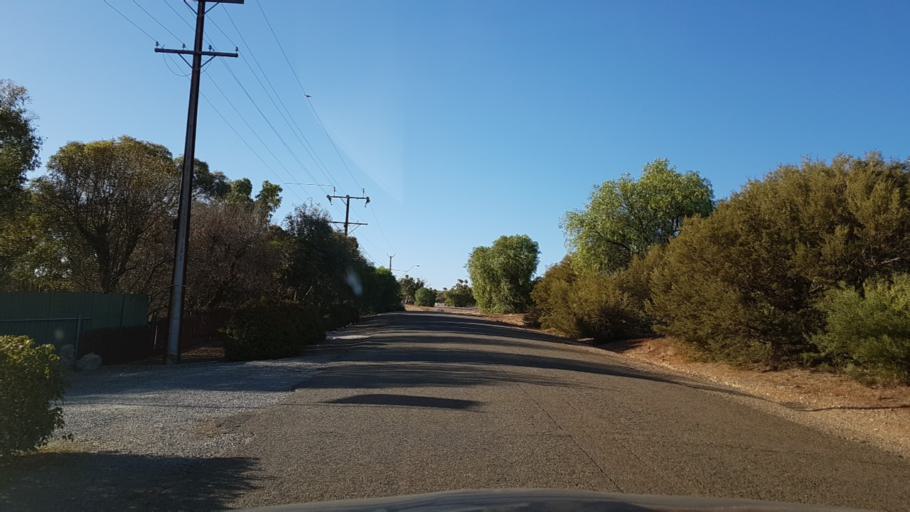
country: AU
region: South Australia
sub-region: Clare and Gilbert Valleys
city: Clare
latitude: -33.6681
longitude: 138.9320
